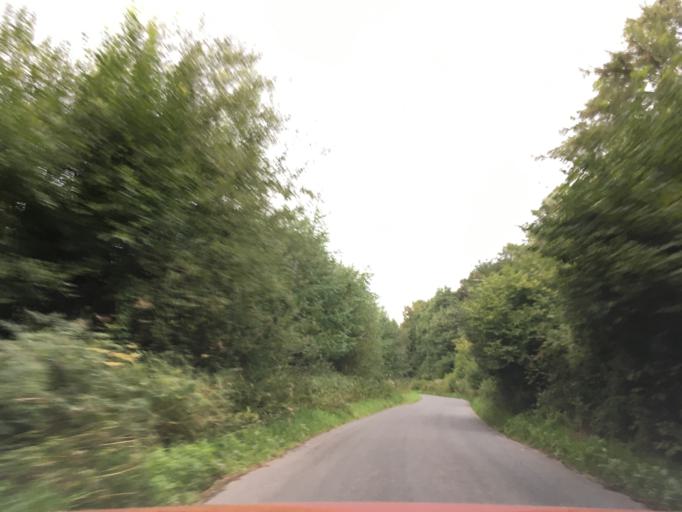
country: GB
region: Wales
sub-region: Newport
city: Llanvaches
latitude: 51.6419
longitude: -2.8275
